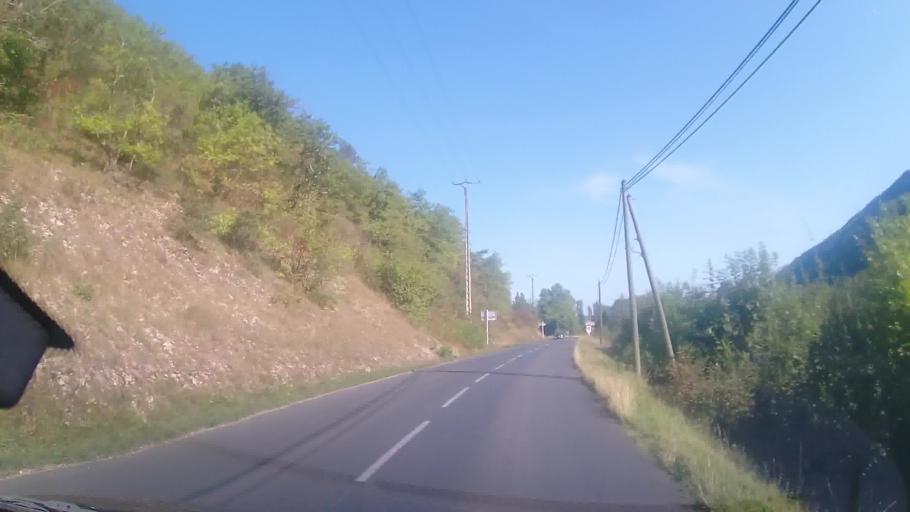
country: FR
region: Aquitaine
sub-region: Departement de la Dordogne
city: Cenac-et-Saint-Julien
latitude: 44.8072
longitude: 1.1538
